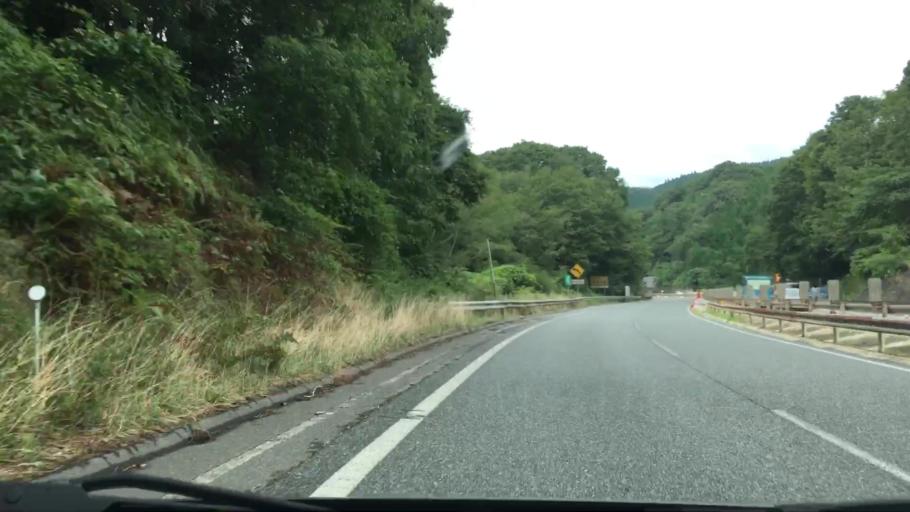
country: JP
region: Okayama
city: Niimi
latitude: 35.0158
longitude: 133.5841
